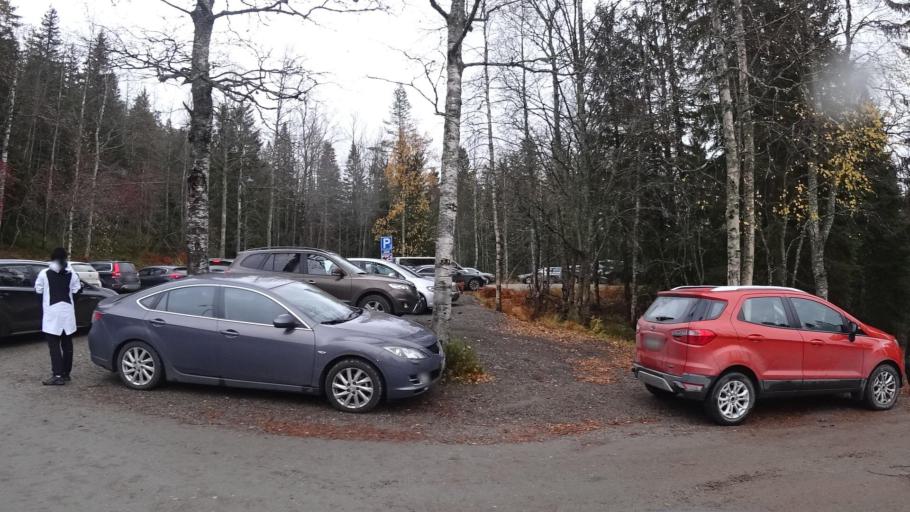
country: FI
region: North Karelia
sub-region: Pielisen Karjala
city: Lieksa
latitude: 63.0945
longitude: 29.8037
